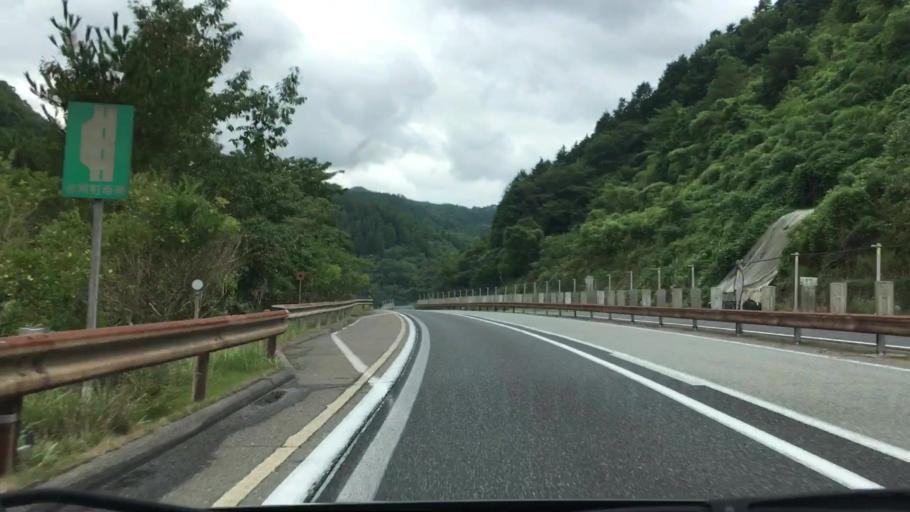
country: JP
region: Okayama
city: Niimi
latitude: 35.0223
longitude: 133.5237
